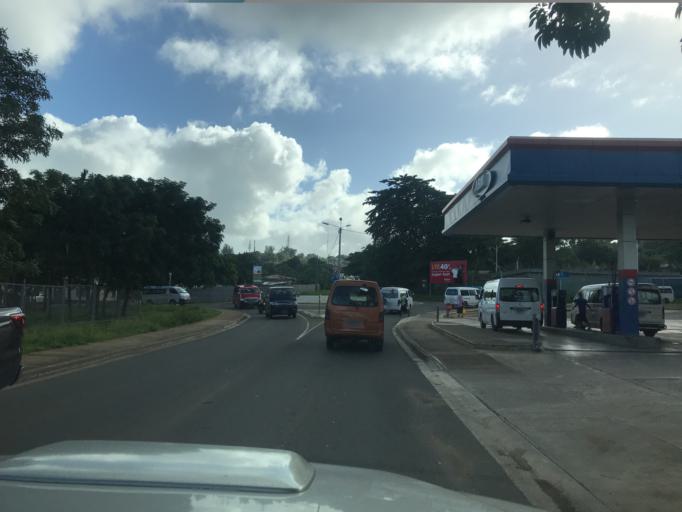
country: VU
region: Shefa
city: Port-Vila
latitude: -17.7436
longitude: 168.3171
